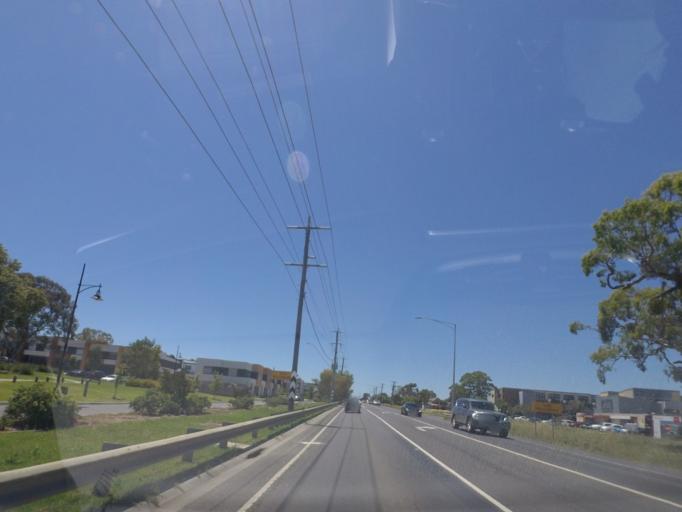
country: AU
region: Victoria
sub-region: Whittlesea
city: Epping
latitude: -37.6310
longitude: 145.0274
